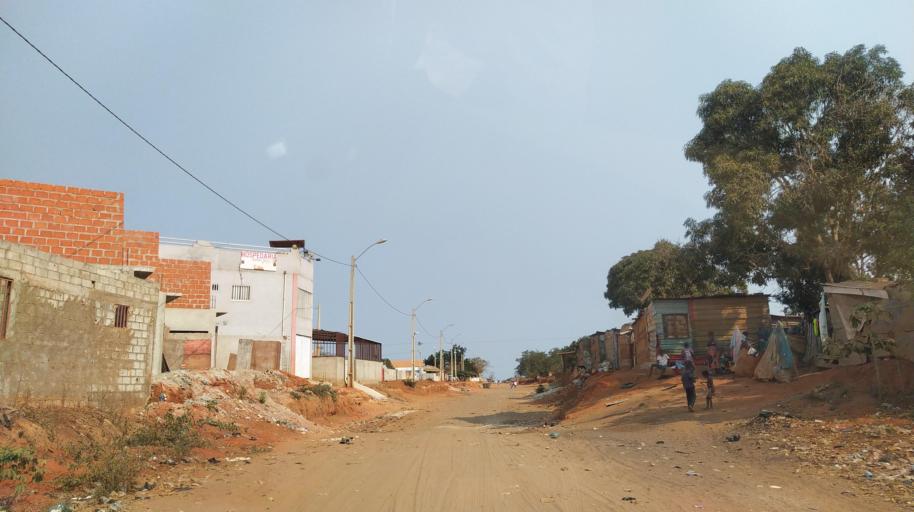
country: AO
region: Luanda
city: Luanda
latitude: -9.0646
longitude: 13.4165
